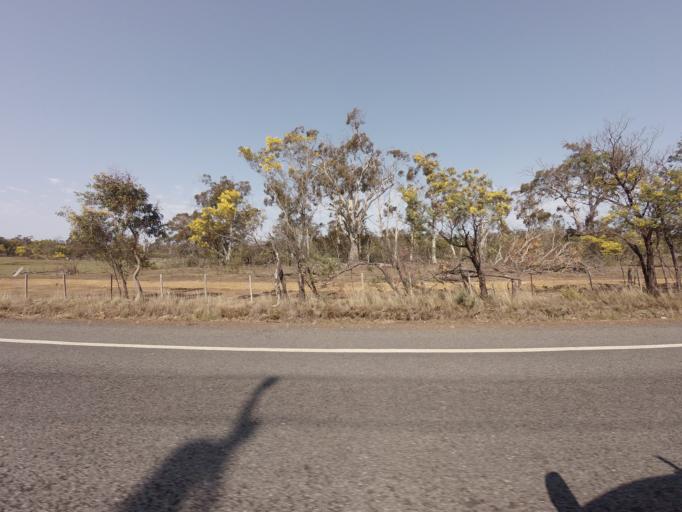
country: AU
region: Tasmania
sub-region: Northern Midlands
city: Evandale
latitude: -41.8319
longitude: 147.4778
